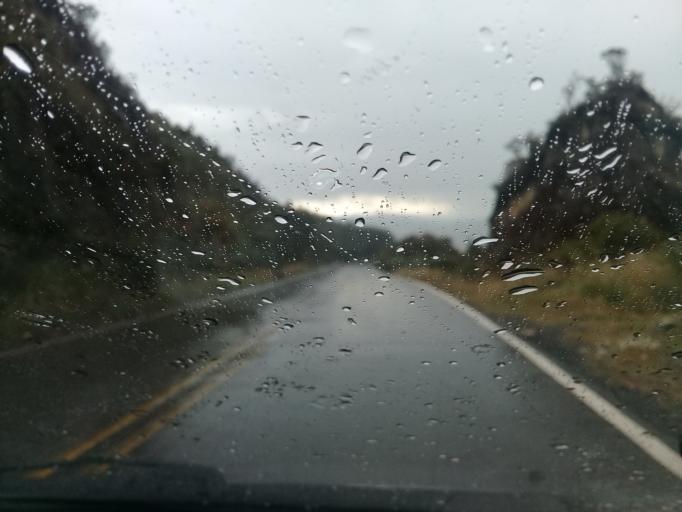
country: CO
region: Cundinamarca
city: Guasca
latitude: 4.8431
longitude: -73.8270
